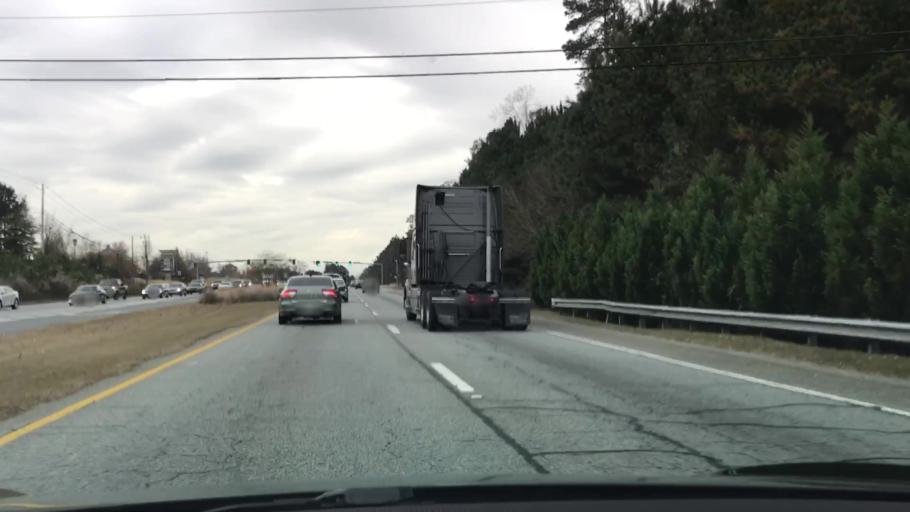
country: US
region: Georgia
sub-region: Gwinnett County
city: Suwanee
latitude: 34.0416
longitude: -84.0983
